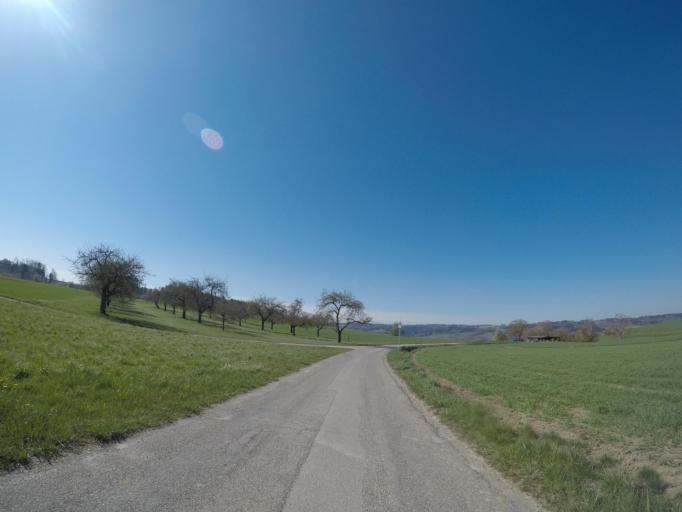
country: DE
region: Baden-Wuerttemberg
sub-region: Tuebingen Region
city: Guggenhausen
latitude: 47.8722
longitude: 9.4489
